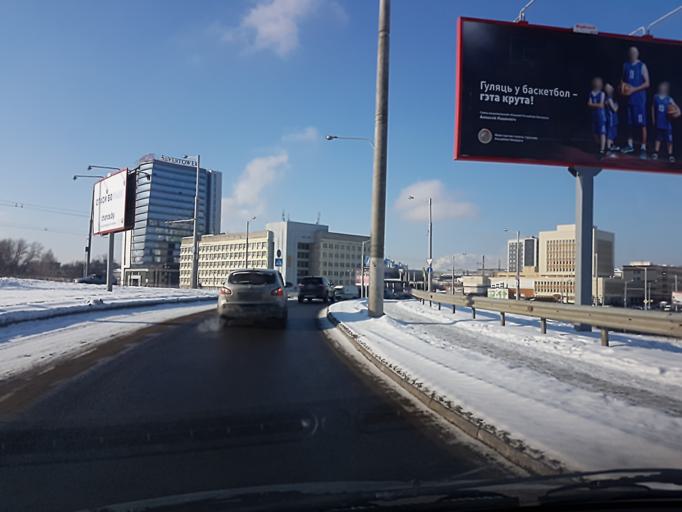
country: BY
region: Minsk
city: Minsk
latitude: 53.9075
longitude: 27.5232
